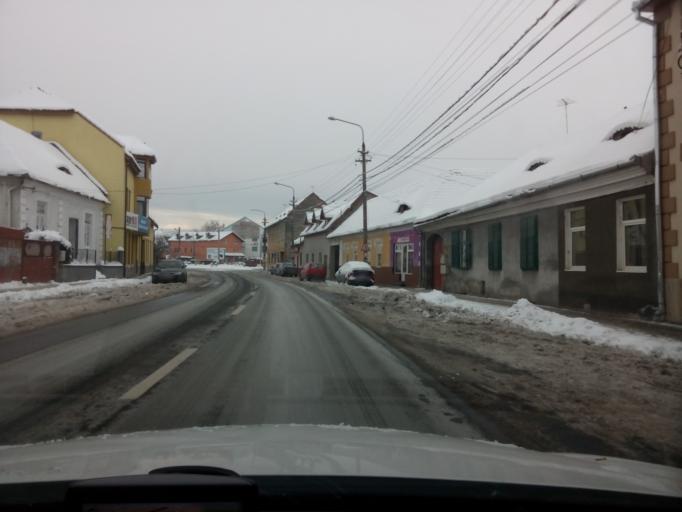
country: RO
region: Sibiu
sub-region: Municipiul Sibiu
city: Sibiu
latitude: 45.8022
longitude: 24.1437
